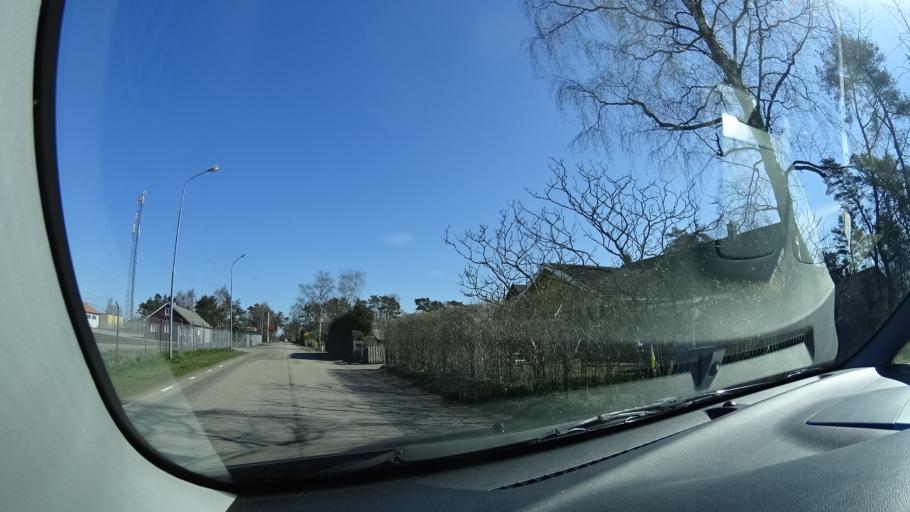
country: SE
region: Skane
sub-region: Hoganas Kommun
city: Hoganas
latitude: 56.2198
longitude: 12.6706
